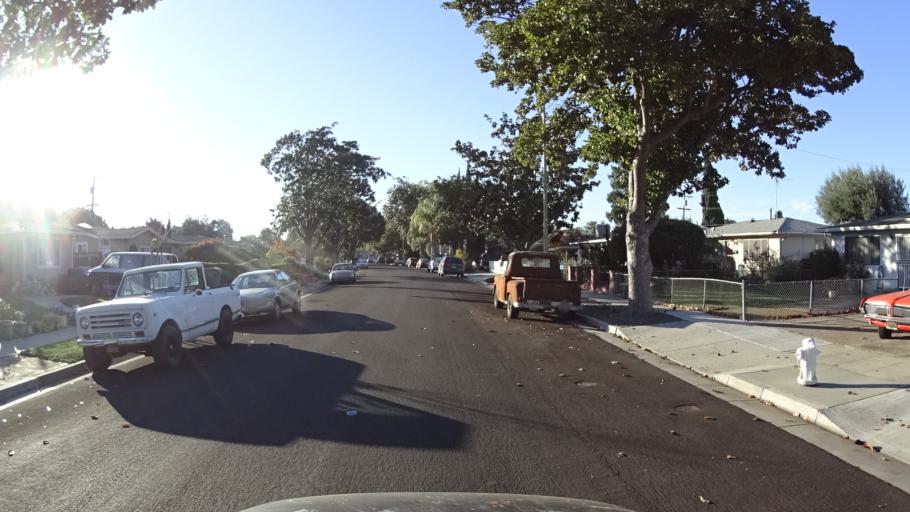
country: US
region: California
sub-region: Santa Clara County
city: Santa Clara
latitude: 37.3683
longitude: -121.9844
